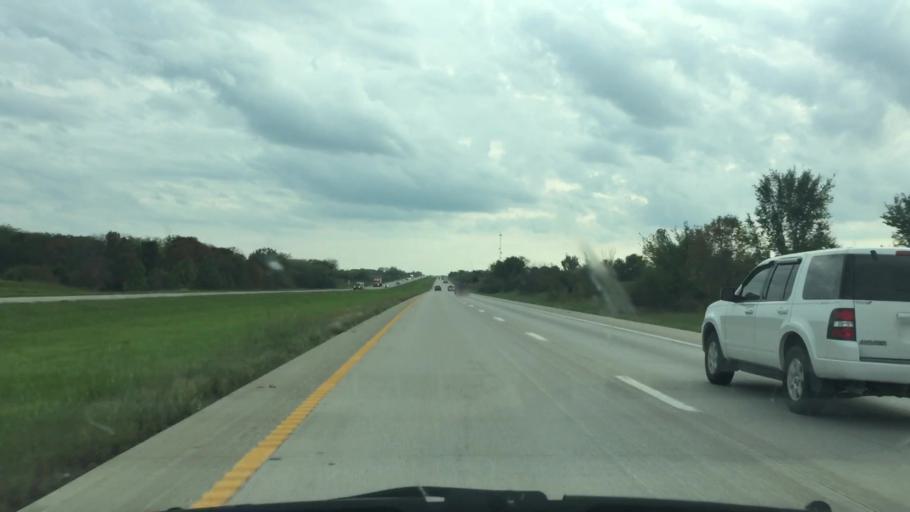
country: US
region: Missouri
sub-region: Clinton County
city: Cameron
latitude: 39.6277
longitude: -94.2459
